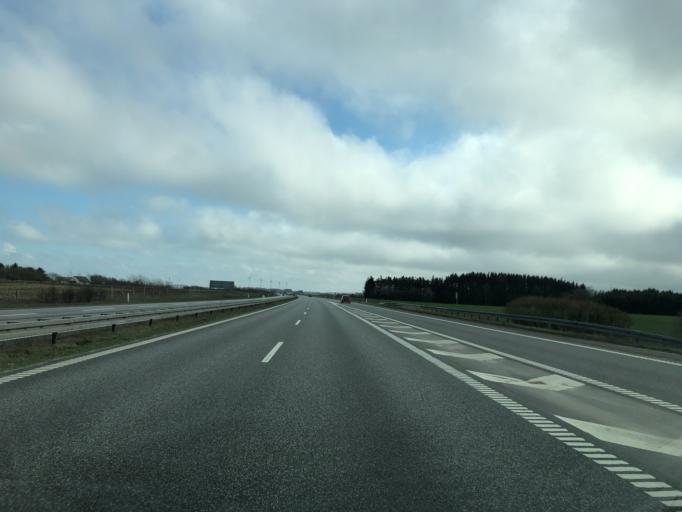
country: DK
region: North Denmark
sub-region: Hjorring Kommune
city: Hjorring
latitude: 57.4201
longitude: 10.0289
